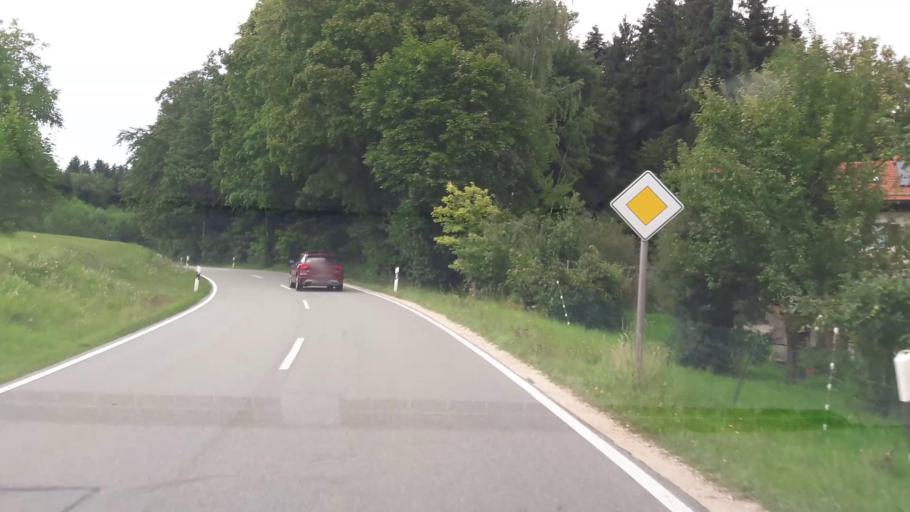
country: DE
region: Bavaria
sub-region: Upper Bavaria
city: Anger
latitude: 47.8076
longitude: 12.8608
